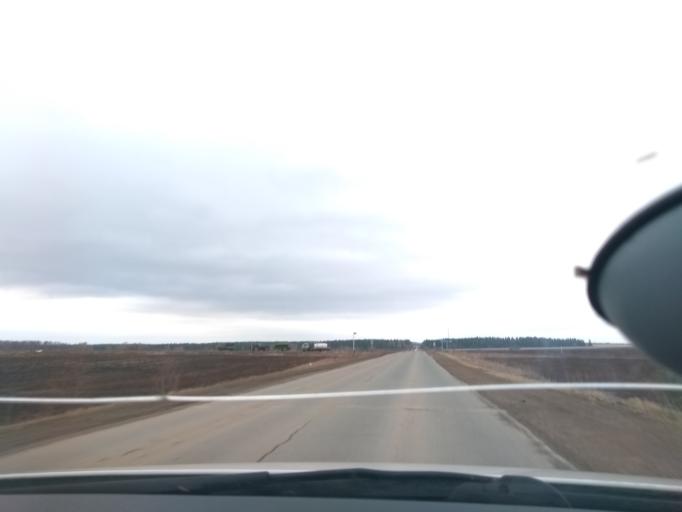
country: RU
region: Perm
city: Kungur
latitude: 57.3861
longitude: 56.8596
